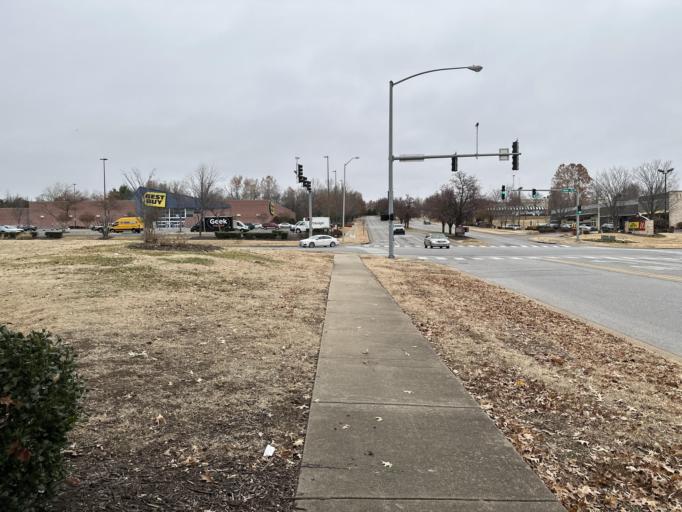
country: US
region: Arkansas
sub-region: Washington County
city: Johnson
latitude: 36.1232
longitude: -94.1501
